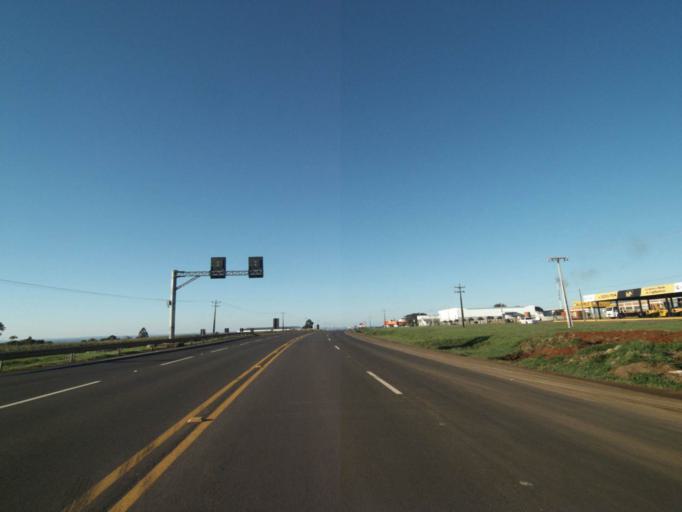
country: BR
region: Parana
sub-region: Mandaguari
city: Mandaguari
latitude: -23.5072
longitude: -51.6998
